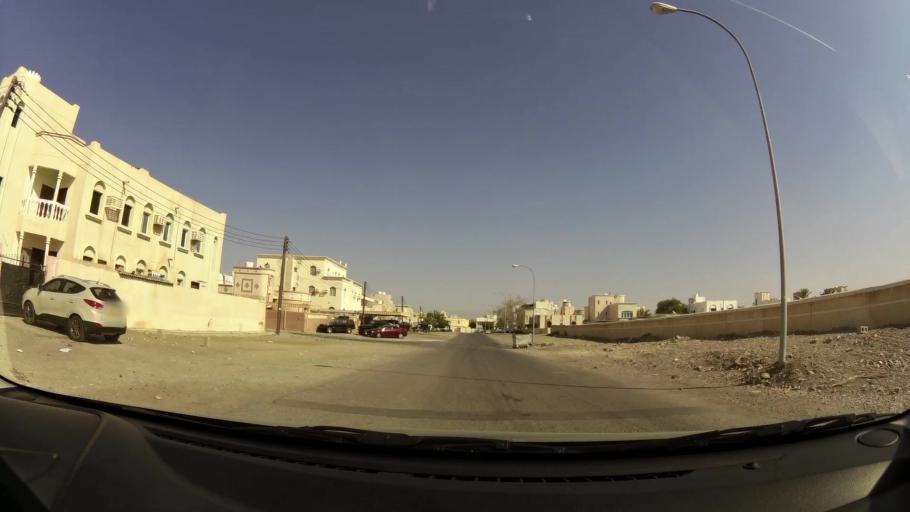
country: OM
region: Muhafazat Masqat
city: As Sib al Jadidah
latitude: 23.6322
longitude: 58.2041
